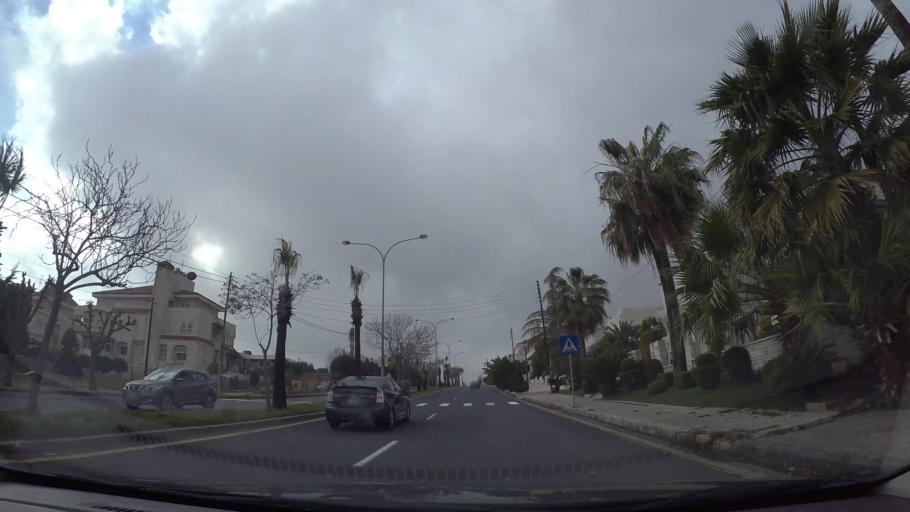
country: JO
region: Amman
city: Al Bunayyat ash Shamaliyah
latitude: 31.9514
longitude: 35.8852
